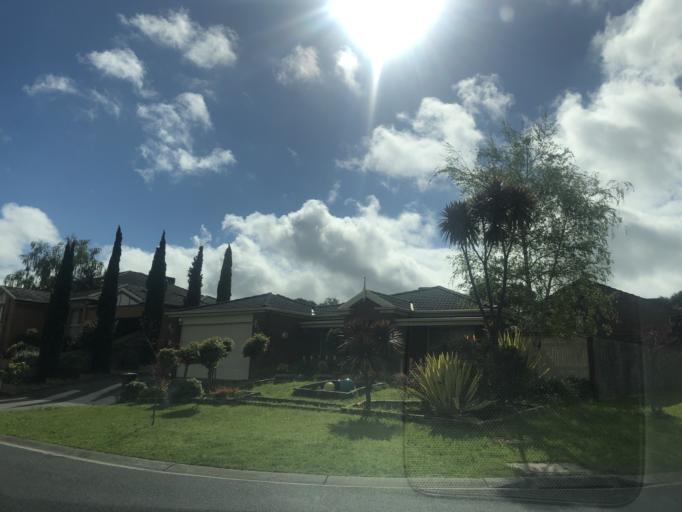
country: AU
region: Victoria
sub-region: Knox
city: Rowville
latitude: -37.9377
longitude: 145.2513
